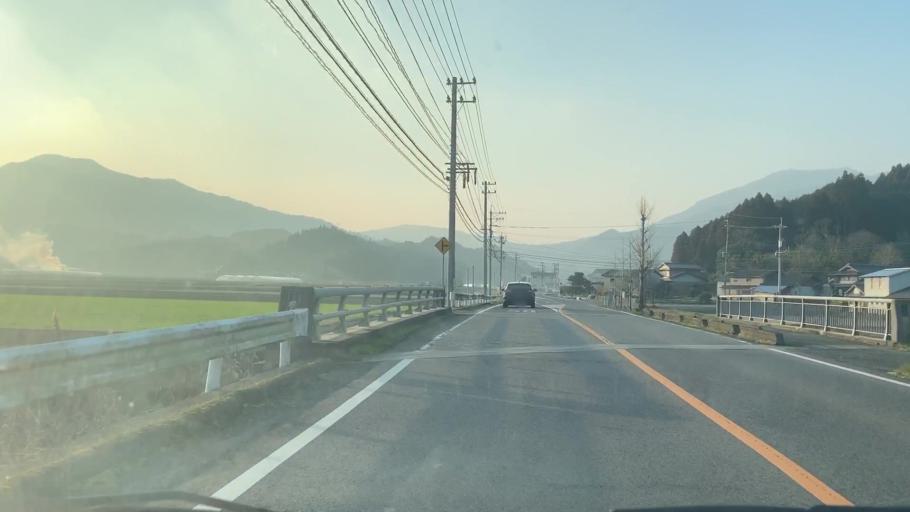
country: JP
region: Saga Prefecture
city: Takeocho-takeo
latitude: 33.2582
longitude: 130.0702
